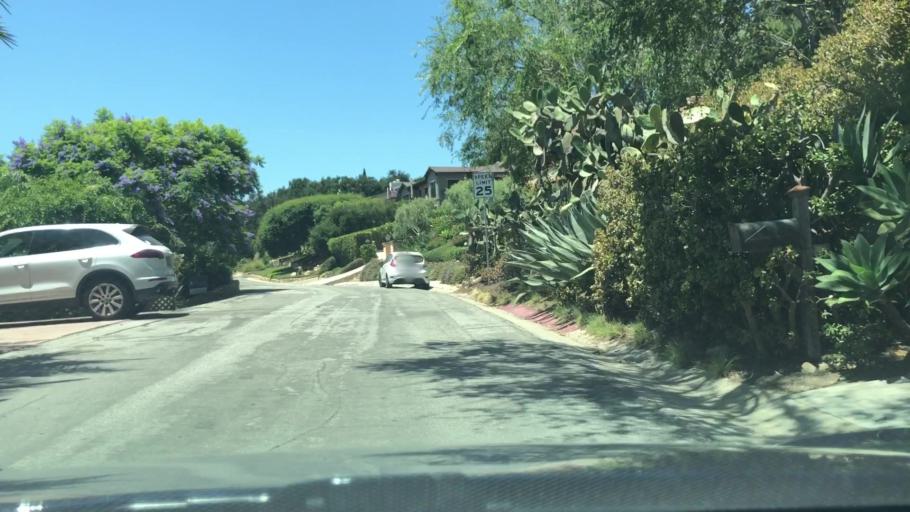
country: US
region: California
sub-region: Santa Barbara County
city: Santa Barbara
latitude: 34.4385
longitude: -119.6950
